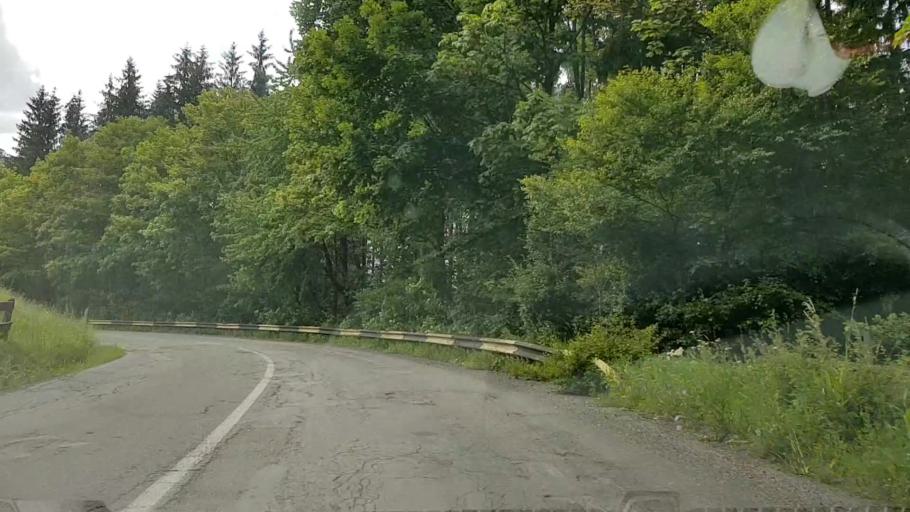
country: RO
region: Neamt
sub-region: Comuna Pangarati
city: Pangarati
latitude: 46.9350
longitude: 26.1245
